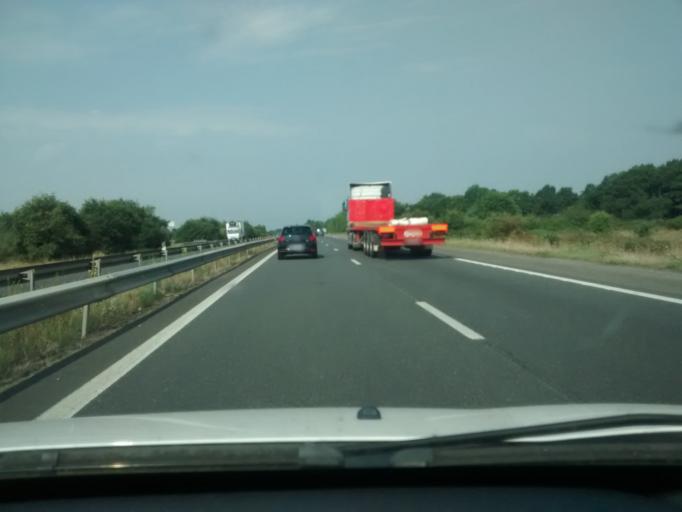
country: FR
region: Pays de la Loire
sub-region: Departement de la Loire-Atlantique
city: Prinquiau
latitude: 47.3566
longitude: -1.9950
